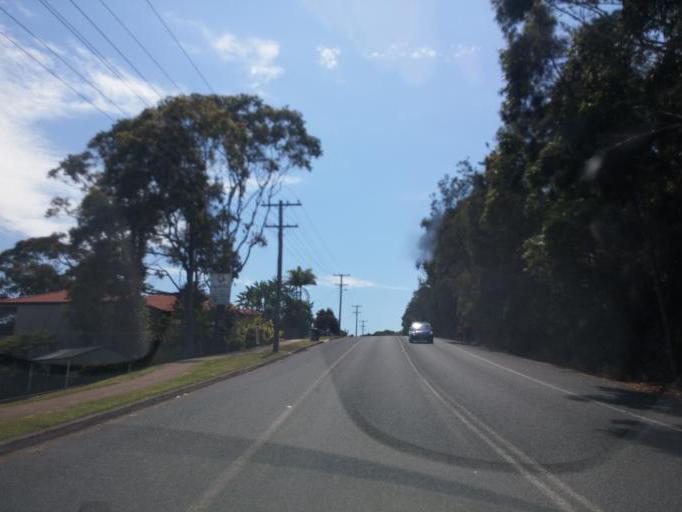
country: AU
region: New South Wales
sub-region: Port Macquarie-Hastings
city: Port Macquarie
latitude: -31.4590
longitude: 152.9296
